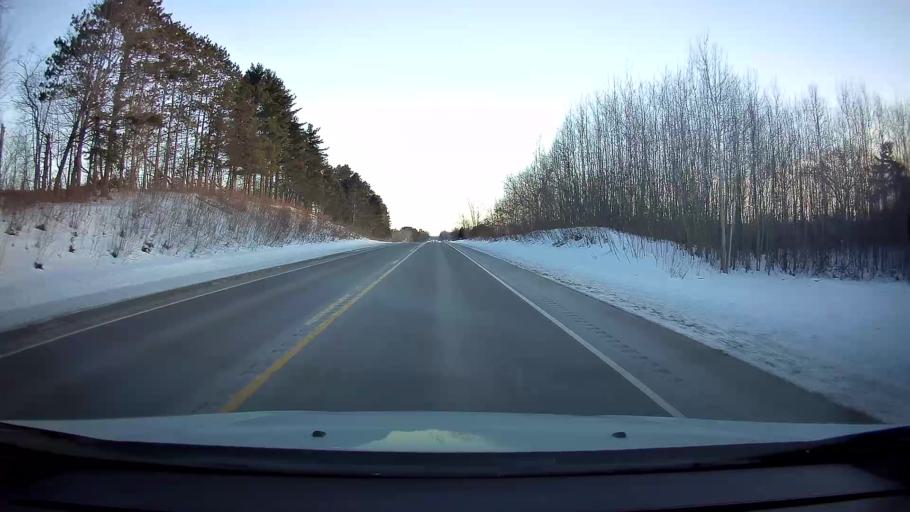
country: US
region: Wisconsin
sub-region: Washburn County
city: Shell Lake
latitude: 45.6806
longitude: -91.9849
